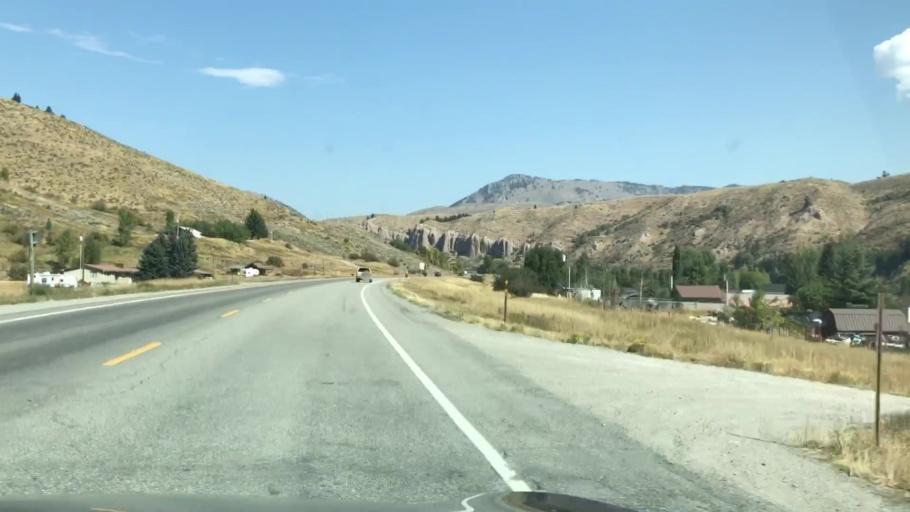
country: US
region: Wyoming
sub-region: Teton County
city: Hoback
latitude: 43.3459
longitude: -110.7221
